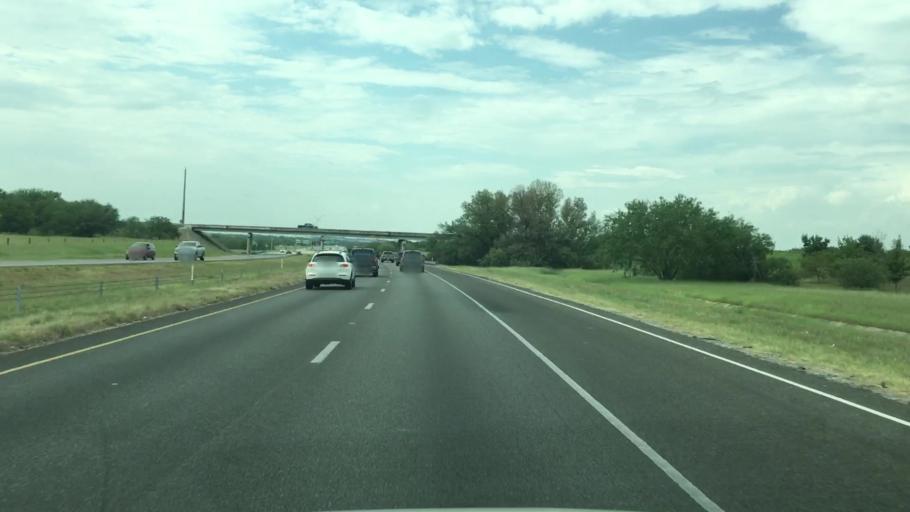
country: US
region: Texas
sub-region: Bexar County
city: Elmendorf
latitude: 29.3059
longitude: -98.3979
